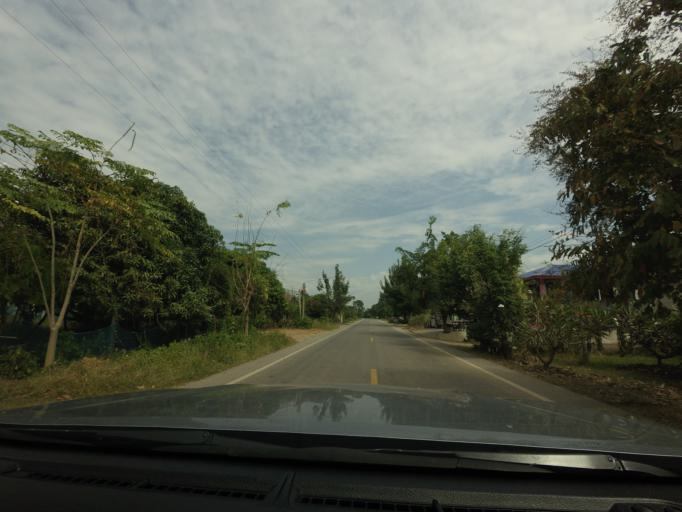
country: TH
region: Phitsanulok
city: Wang Thong
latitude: 16.7219
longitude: 100.3705
